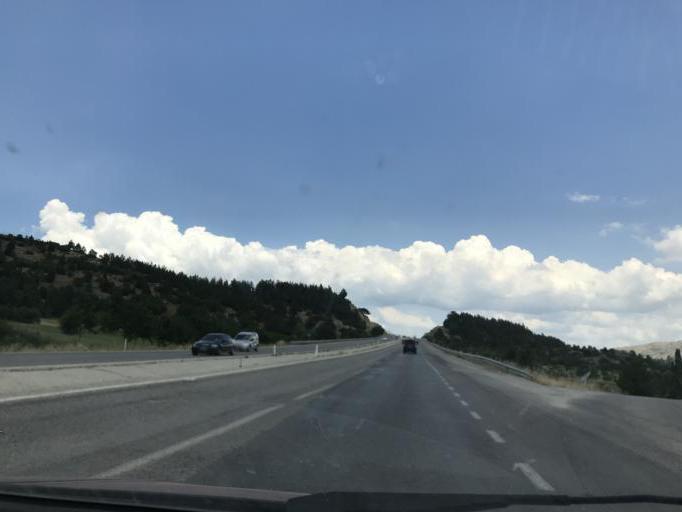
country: TR
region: Denizli
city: Tavas
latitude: 37.6139
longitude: 29.1587
